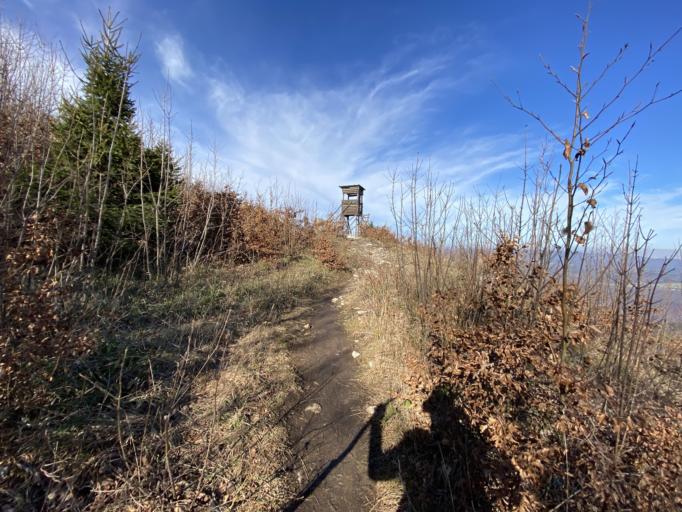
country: AT
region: Lower Austria
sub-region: Politischer Bezirk Baden
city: Heiligenkreuz
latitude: 48.0068
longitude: 16.1401
